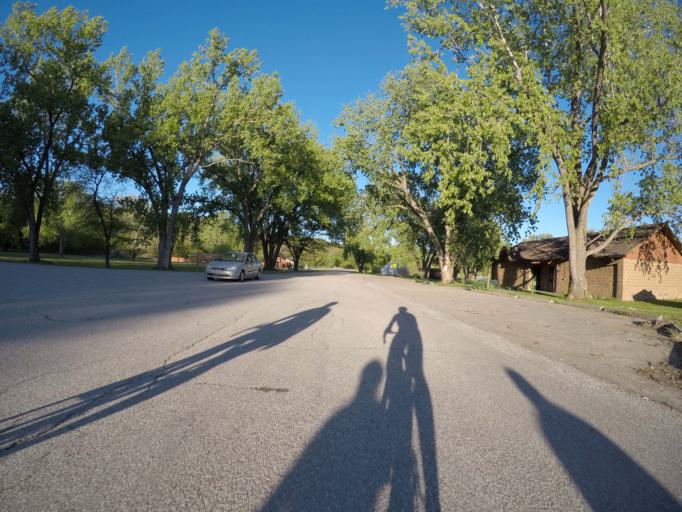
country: US
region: Kansas
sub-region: Riley County
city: Manhattan
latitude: 39.2556
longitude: -96.5797
